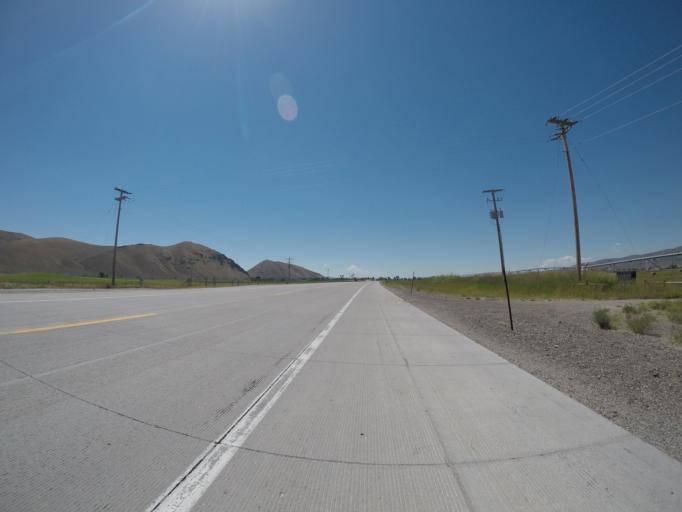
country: US
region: Idaho
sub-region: Bear Lake County
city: Montpelier
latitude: 42.1100
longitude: -110.9558
